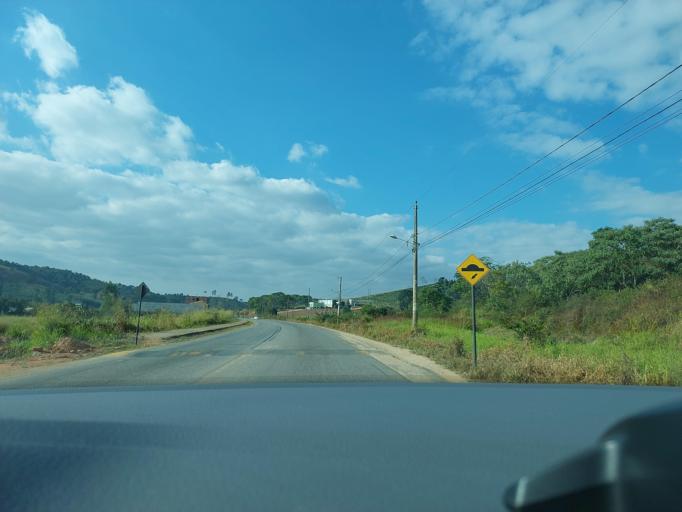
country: BR
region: Minas Gerais
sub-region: Vicosa
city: Vicosa
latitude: -20.8387
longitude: -42.8008
